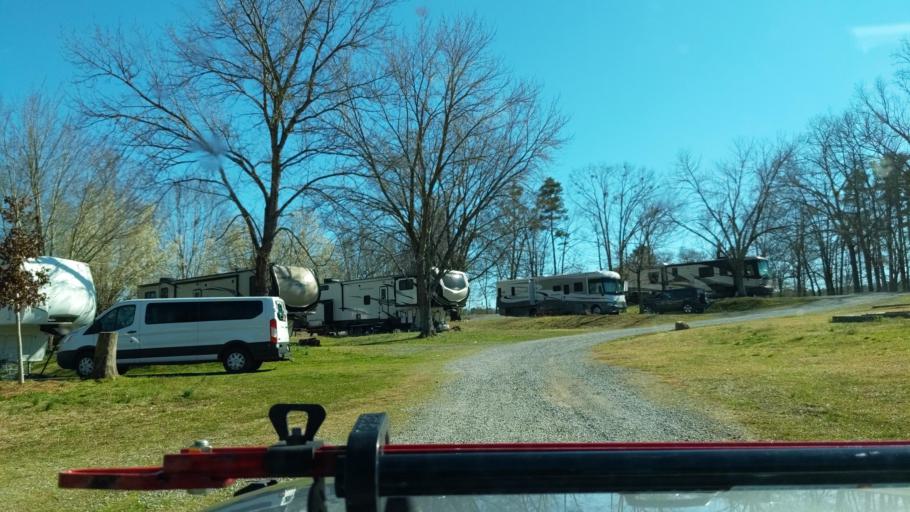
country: US
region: Alabama
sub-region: Walker County
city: Jasper
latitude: 34.0539
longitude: -87.1440
